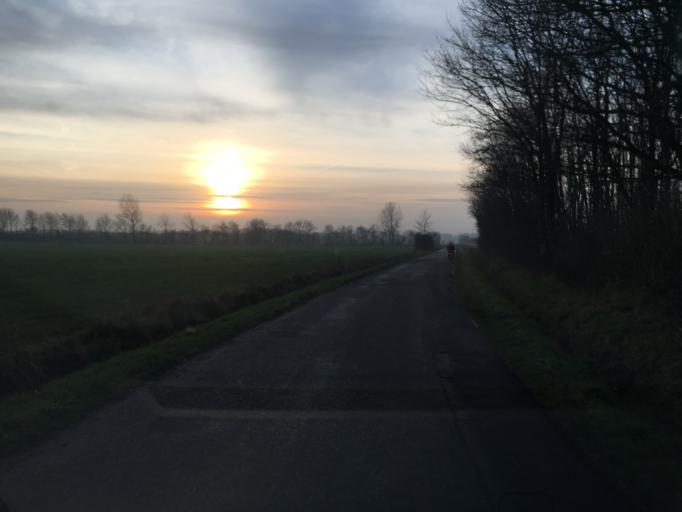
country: DK
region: South Denmark
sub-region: Tonder Kommune
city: Toftlund
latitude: 55.1393
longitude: 9.0313
